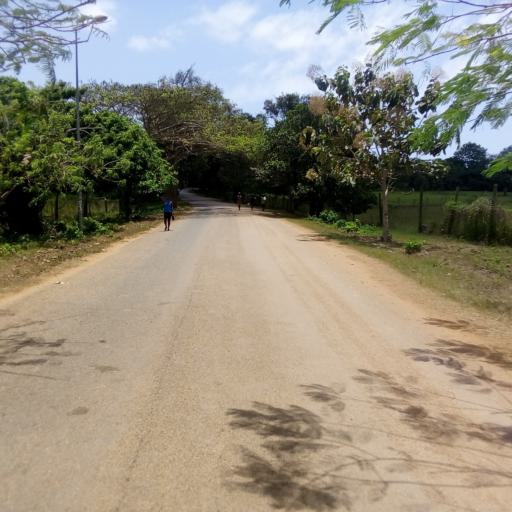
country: GH
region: Central
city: Cape Coast
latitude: 5.1319
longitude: -1.2913
